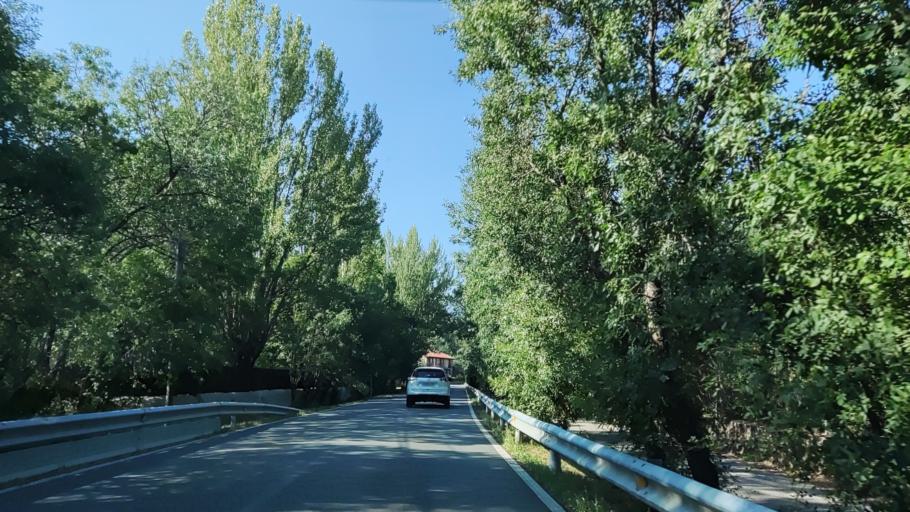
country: ES
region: Madrid
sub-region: Provincia de Madrid
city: Rascafria
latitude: 40.8979
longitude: -3.8803
